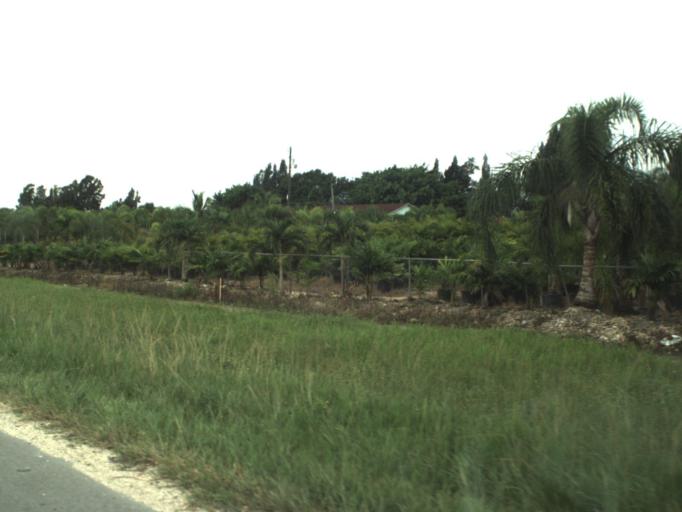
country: US
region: Florida
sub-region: Miami-Dade County
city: The Hammocks
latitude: 25.6802
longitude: -80.4797
